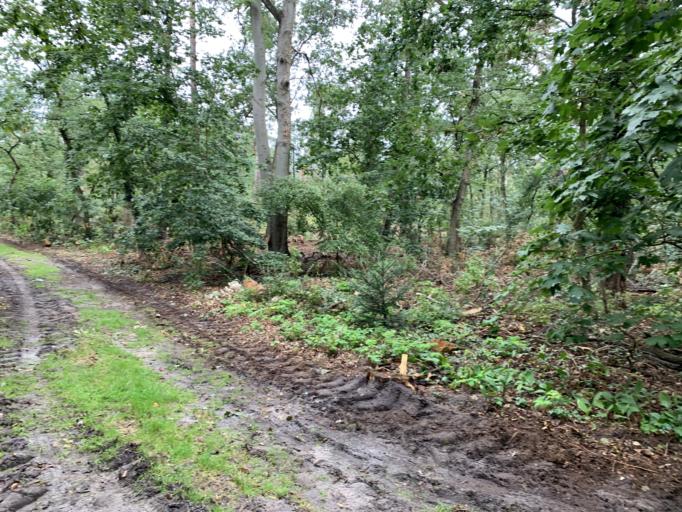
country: DE
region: Brandenburg
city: Wusterwitz
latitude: 52.4040
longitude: 12.4091
